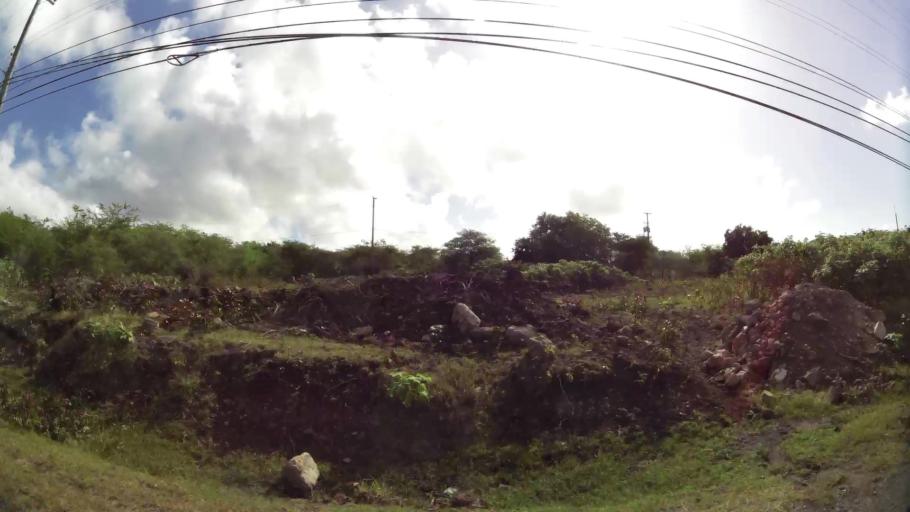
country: KN
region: Saint Paul Charlestown
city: Charlestown
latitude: 17.1192
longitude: -62.6192
